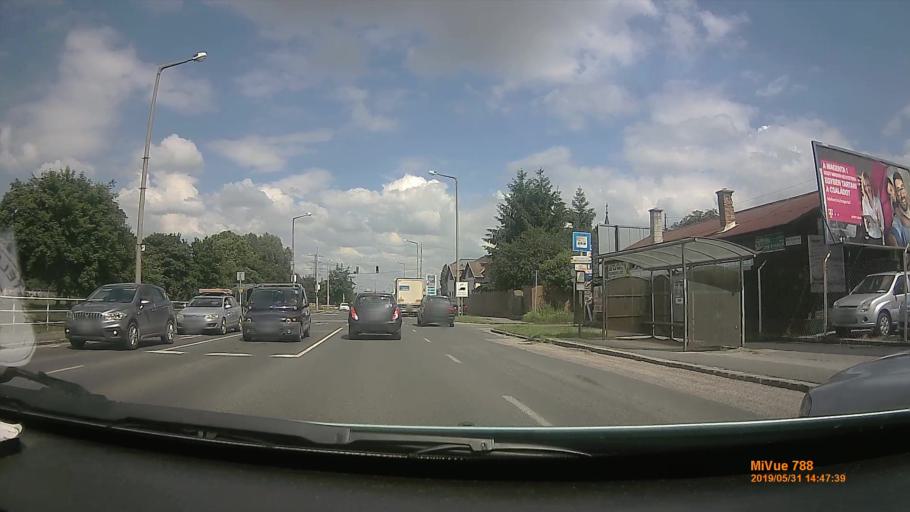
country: HU
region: Borsod-Abauj-Zemplen
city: Miskolc
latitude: 48.1006
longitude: 20.7480
